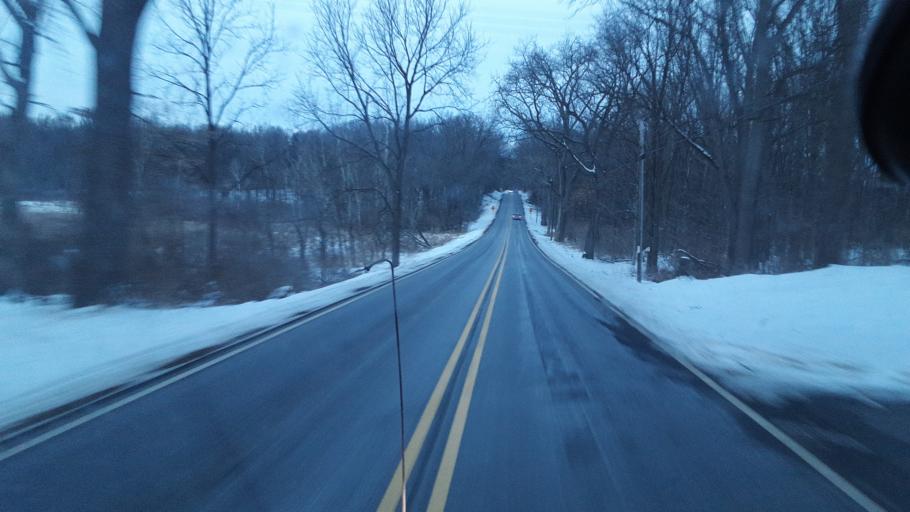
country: US
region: Michigan
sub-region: Jackson County
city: Grass Lake
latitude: 42.3208
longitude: -84.2096
